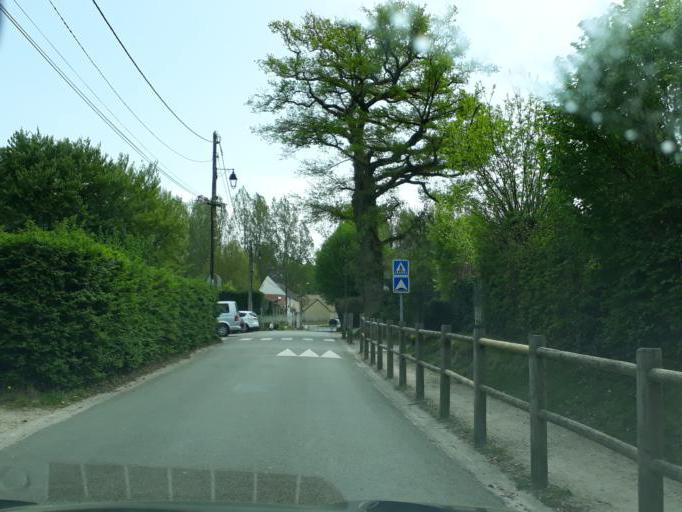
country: FR
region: Ile-de-France
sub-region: Departement des Yvelines
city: Gambais
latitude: 48.7755
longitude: 1.6763
